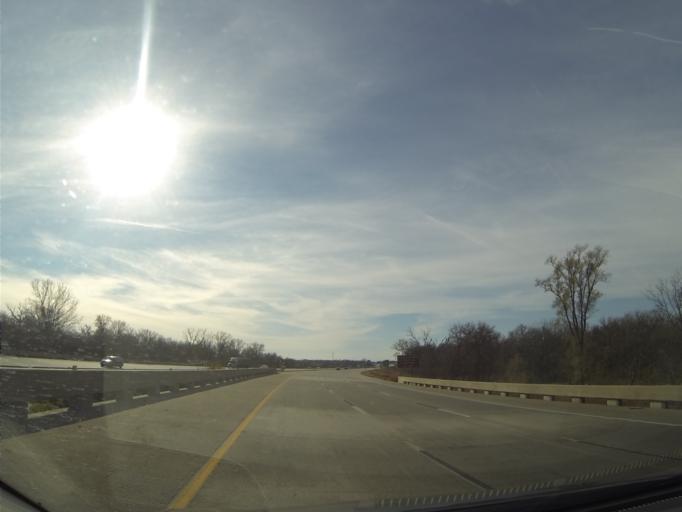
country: US
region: Nebraska
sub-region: Saunders County
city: Ashland
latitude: 41.0327
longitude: -96.2922
